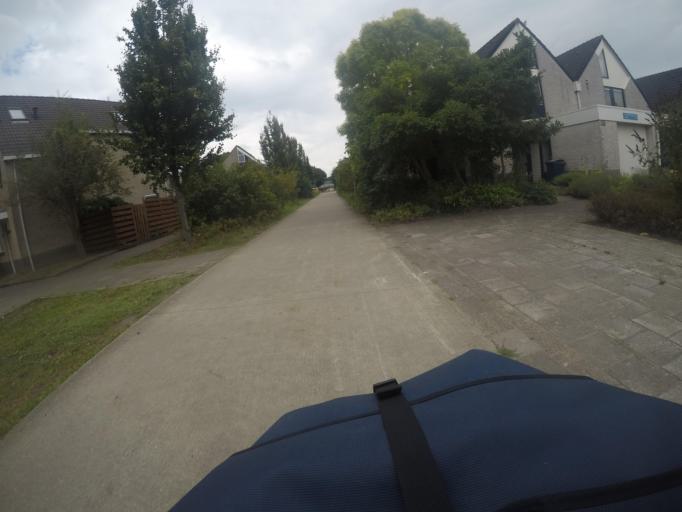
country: NL
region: Flevoland
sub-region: Gemeente Almere
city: Almere Stad
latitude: 52.3626
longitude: 5.1951
